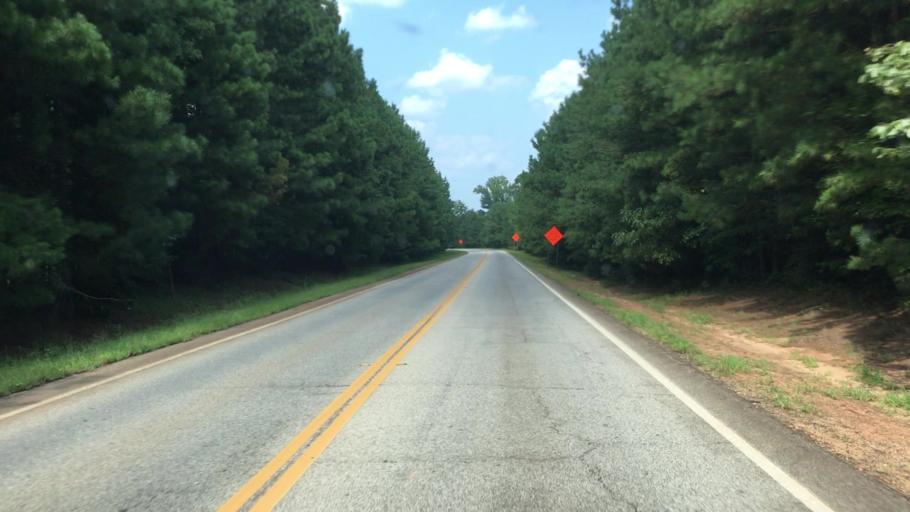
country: US
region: Georgia
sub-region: Monroe County
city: Forsyth
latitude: 33.1046
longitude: -83.8752
